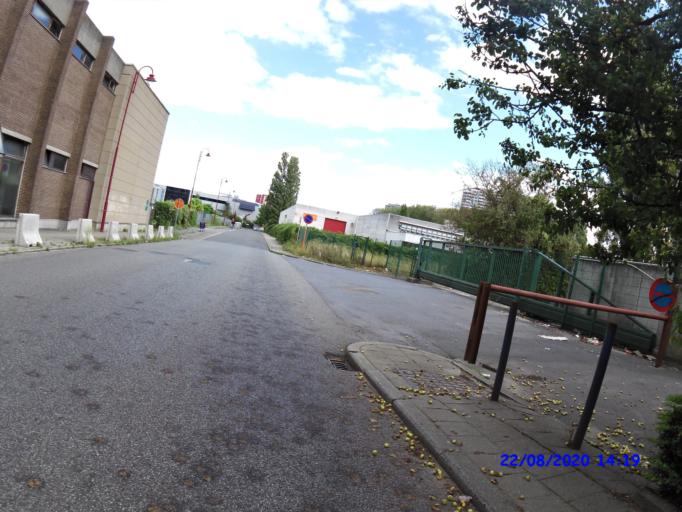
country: BE
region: Flanders
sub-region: Provincie Vlaams-Brabant
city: Wemmel
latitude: 50.8731
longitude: 4.2922
